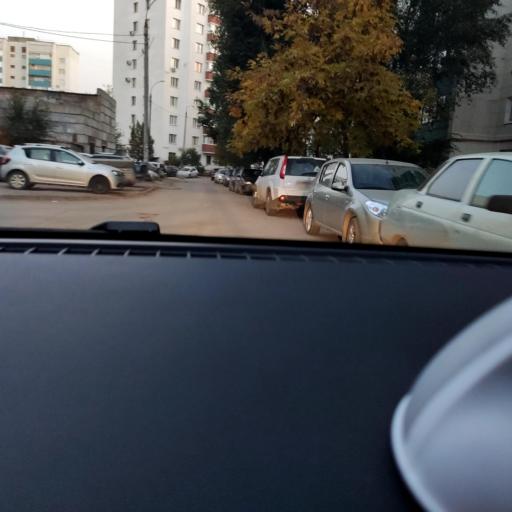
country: RU
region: Samara
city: Petra-Dubrava
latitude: 53.2280
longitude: 50.2734
